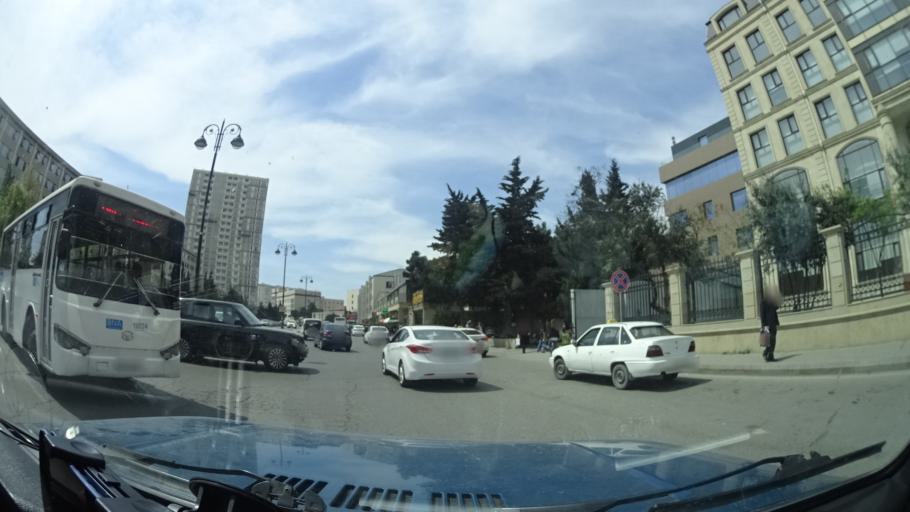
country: AZ
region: Baki
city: Khodzhi-Gasan
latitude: 40.4030
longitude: 49.8068
